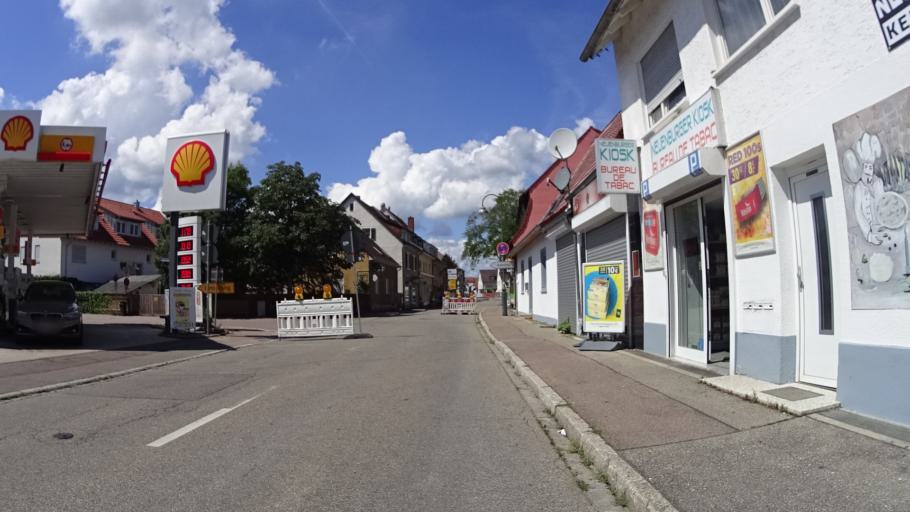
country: DE
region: Baden-Wuerttemberg
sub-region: Freiburg Region
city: Neuenburg am Rhein
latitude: 47.8132
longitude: 7.5638
